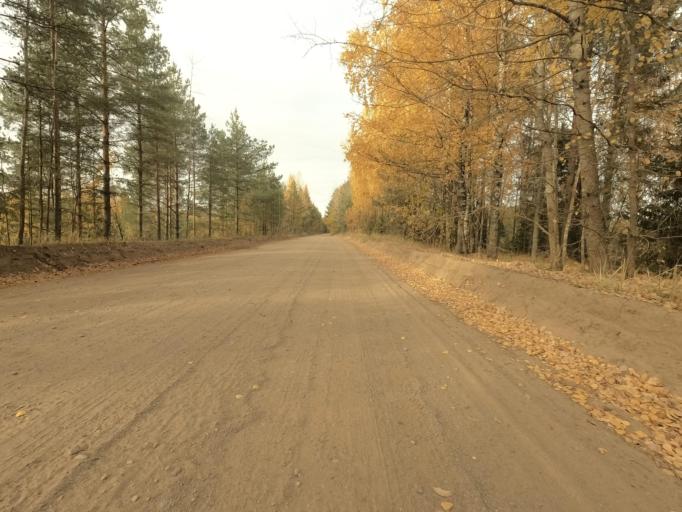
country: RU
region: Leningrad
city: Priladozhskiy
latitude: 59.6766
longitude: 31.3657
